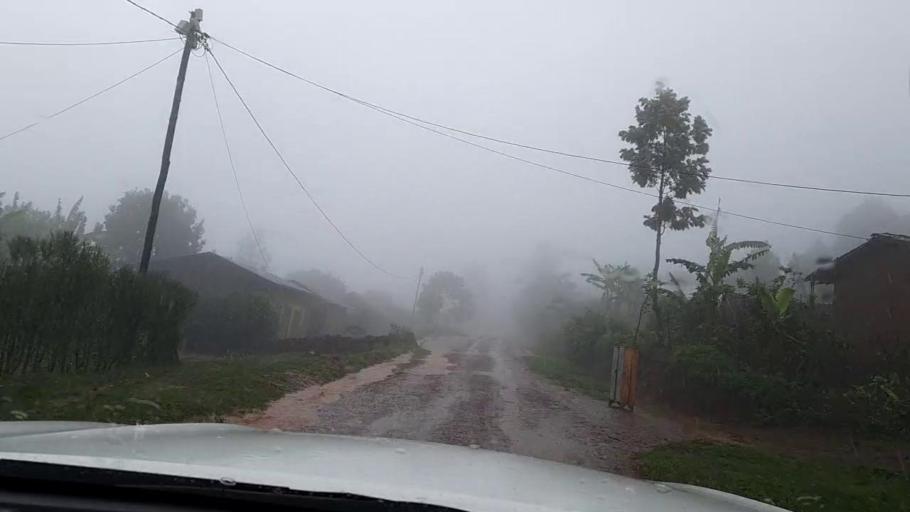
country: RW
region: Northern Province
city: Byumba
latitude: -1.7321
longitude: 30.0154
